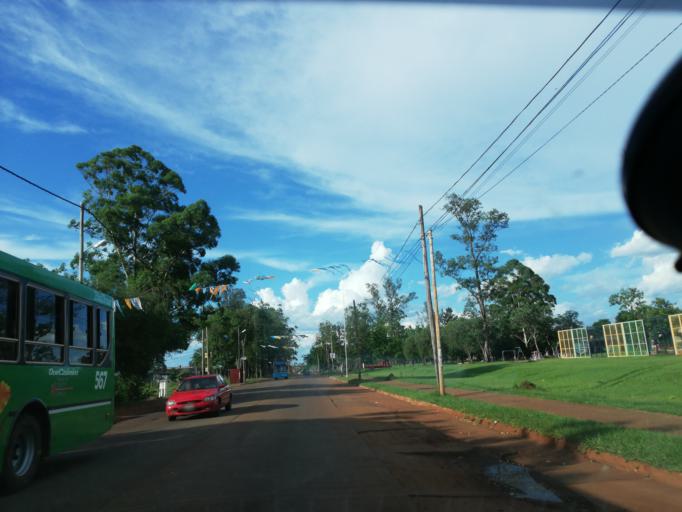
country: AR
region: Misiones
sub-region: Departamento de Capital
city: Posadas
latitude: -27.4077
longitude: -55.9540
